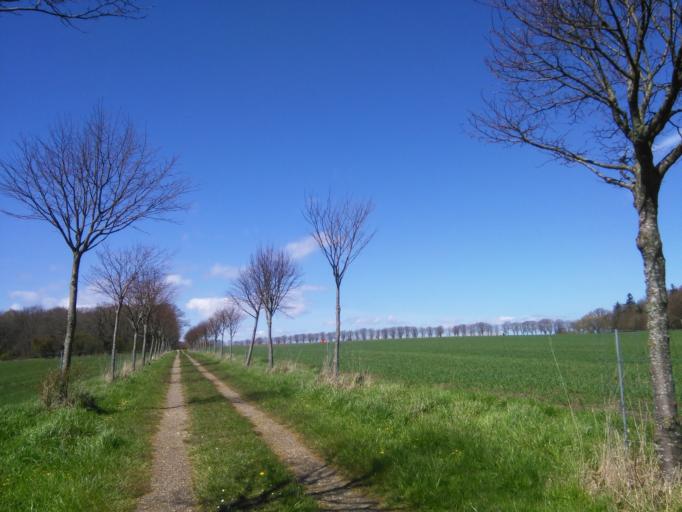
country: DK
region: Central Jutland
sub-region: Hedensted Kommune
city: Juelsminde
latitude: 55.7417
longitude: 10.0410
